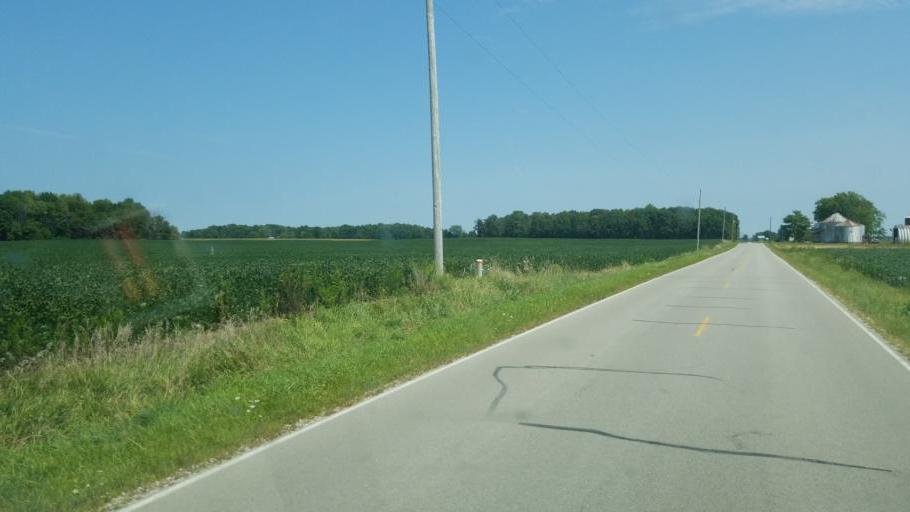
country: US
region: Ohio
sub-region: Crawford County
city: Bucyrus
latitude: 40.8920
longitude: -83.0826
